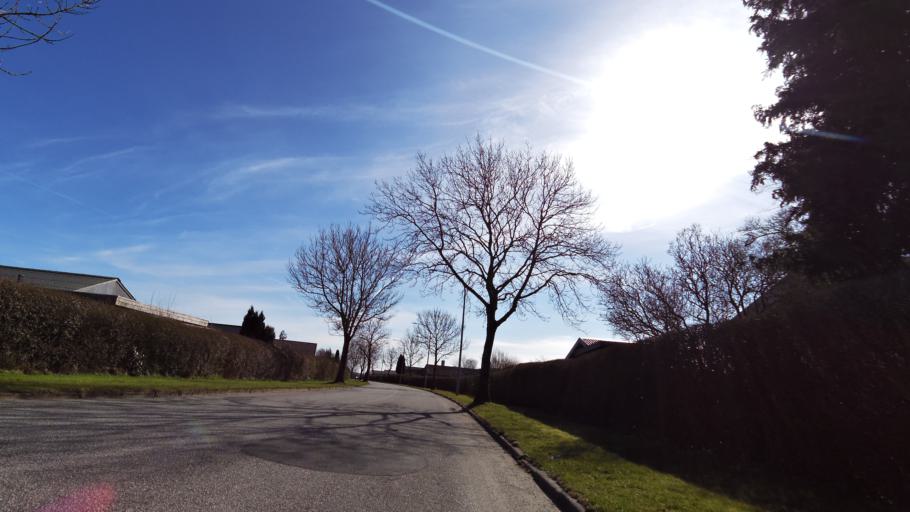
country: DK
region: Central Jutland
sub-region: Arhus Kommune
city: Stavtrup
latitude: 56.1801
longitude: 10.1008
